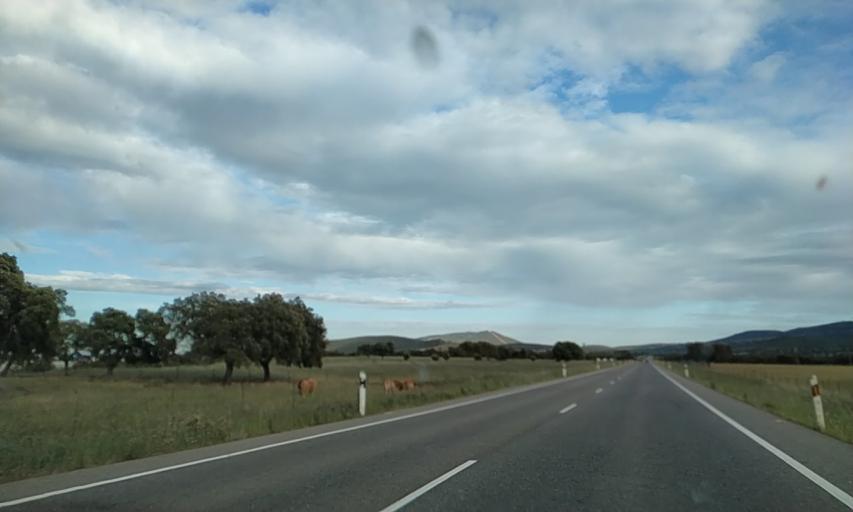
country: ES
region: Extremadura
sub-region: Provincia de Caceres
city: Torrejoncillo
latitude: 39.8684
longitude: -6.4382
